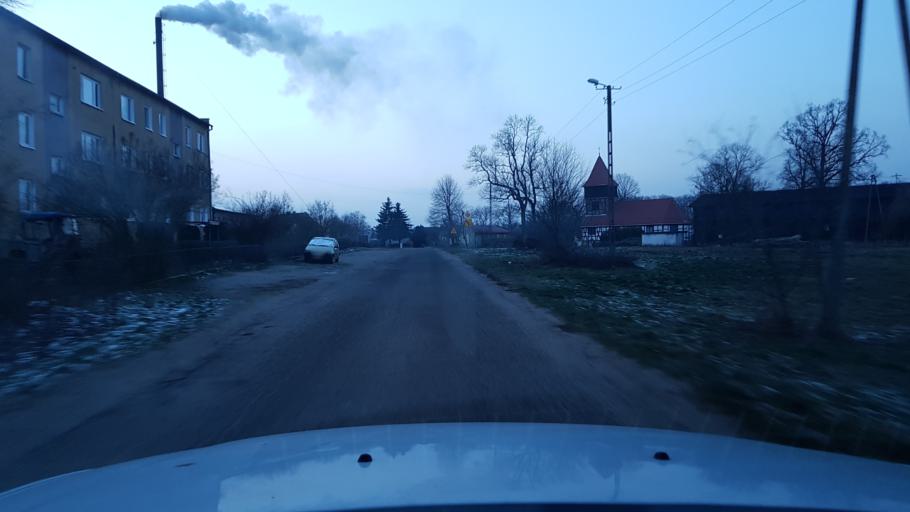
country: PL
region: West Pomeranian Voivodeship
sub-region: Powiat swidwinski
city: Slawoborze
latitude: 53.9473
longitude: 15.7269
